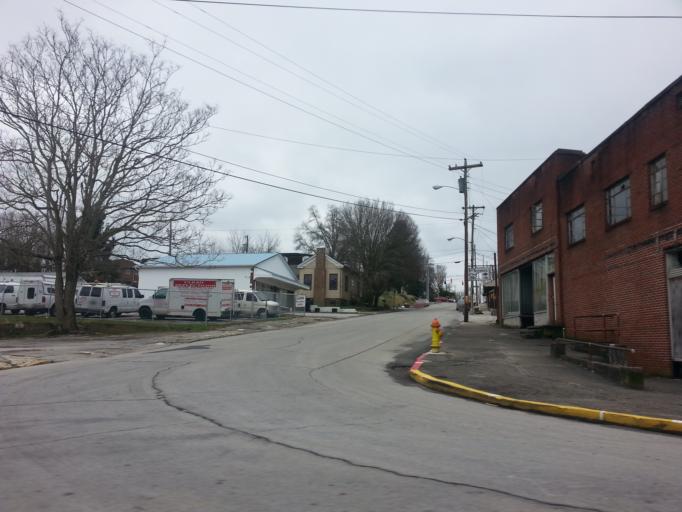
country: US
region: Tennessee
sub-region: Jefferson County
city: Jefferson City
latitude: 36.1274
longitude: -83.4902
